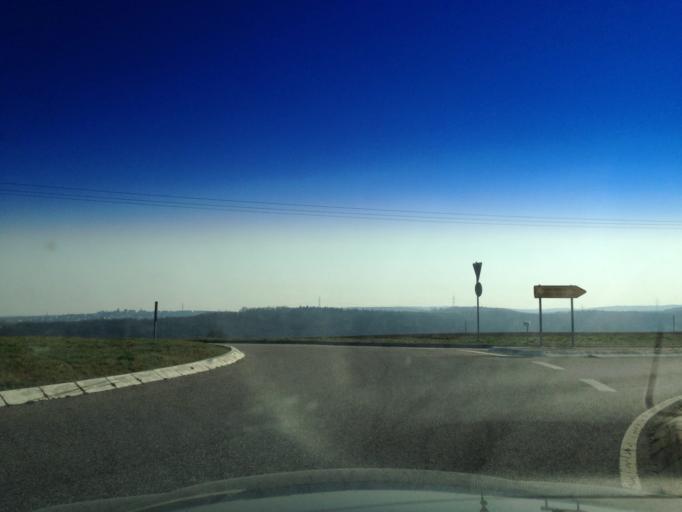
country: DE
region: Baden-Wuerttemberg
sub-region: Regierungsbezirk Stuttgart
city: Vaihingen an der Enz
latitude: 48.9222
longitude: 8.9312
